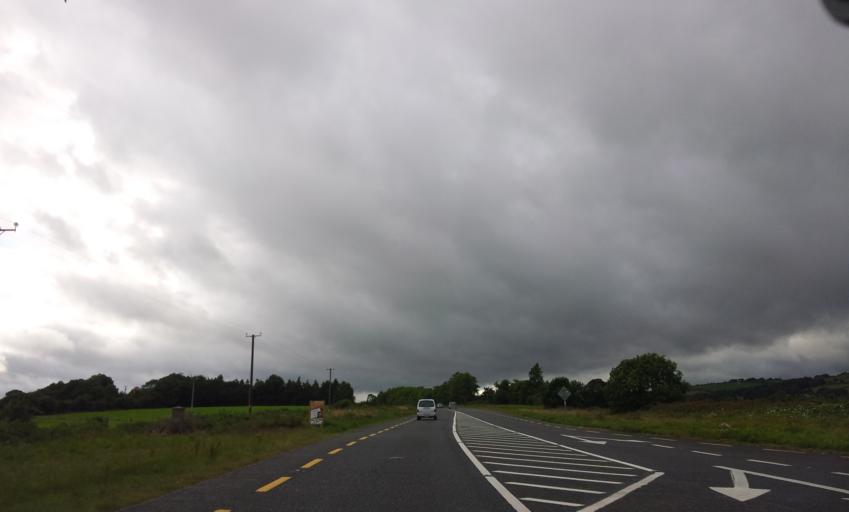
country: IE
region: Munster
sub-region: County Cork
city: Youghal
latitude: 51.9389
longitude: -7.9276
